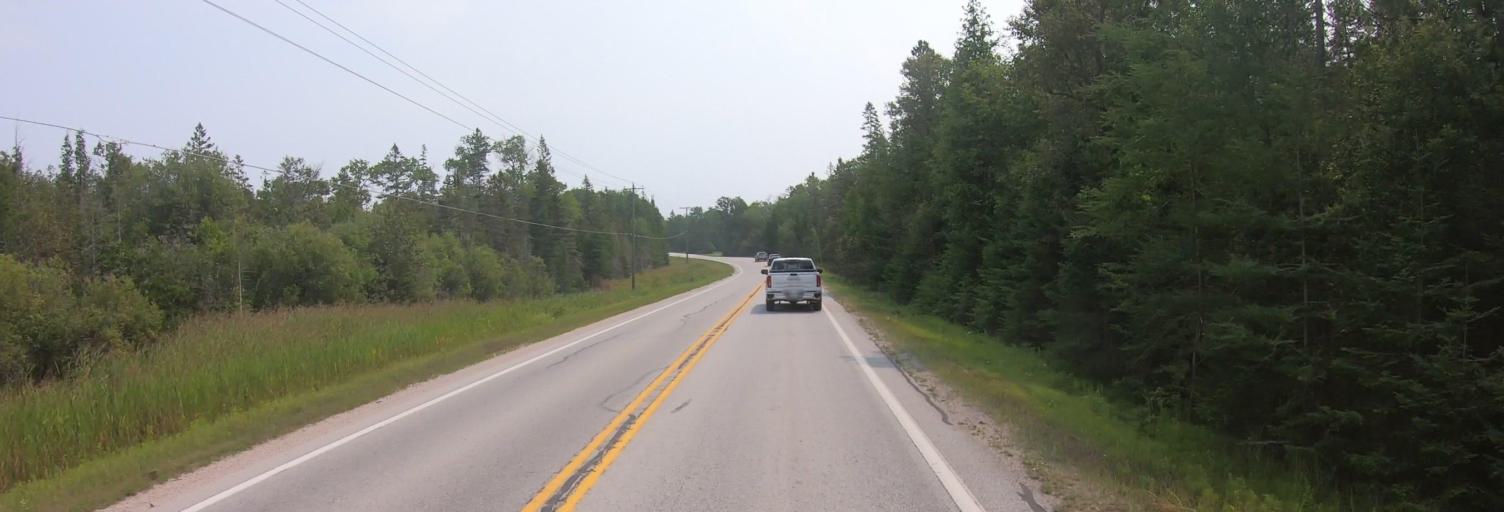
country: CA
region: Ontario
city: Thessalon
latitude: 45.9991
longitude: -83.7631
